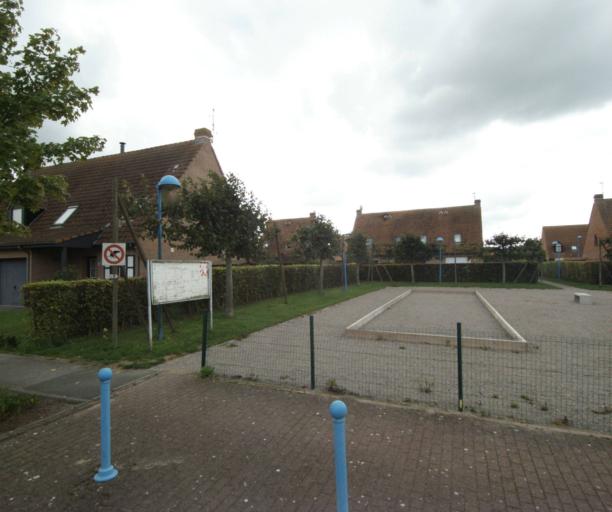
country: FR
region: Nord-Pas-de-Calais
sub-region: Departement du Nord
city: Perenchies
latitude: 50.6638
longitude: 2.9630
